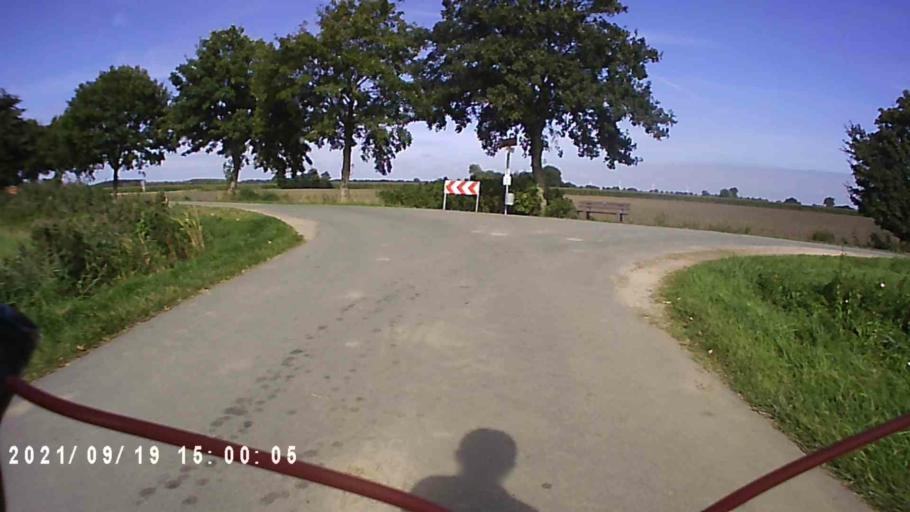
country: DE
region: Lower Saxony
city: Bunde
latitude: 53.1567
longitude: 7.2091
